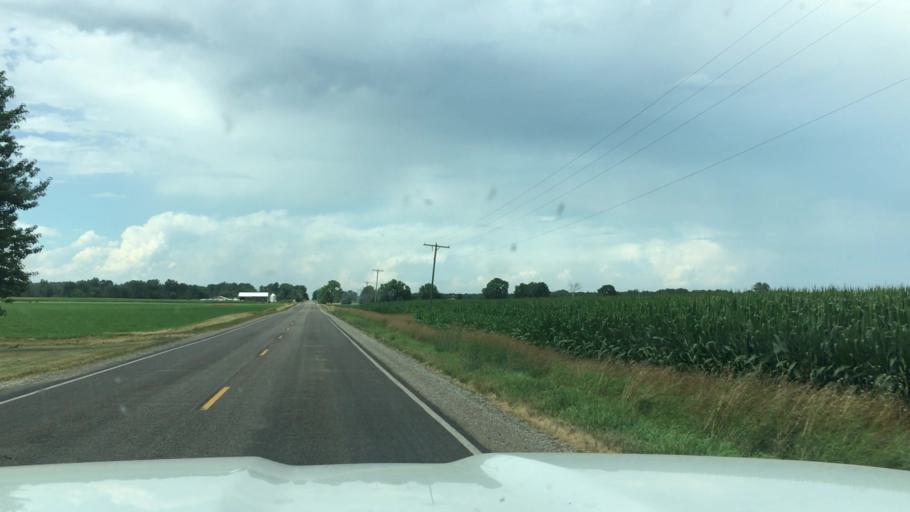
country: US
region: Michigan
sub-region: Montcalm County
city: Carson City
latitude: 43.2252
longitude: -84.7776
